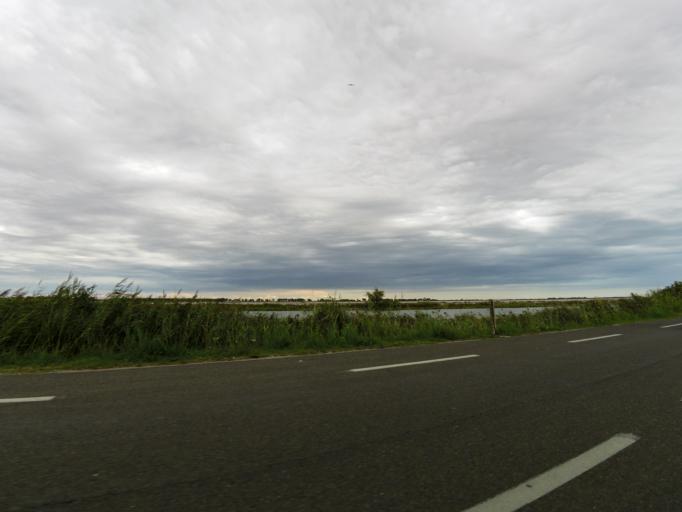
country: FR
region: Languedoc-Roussillon
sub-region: Departement du Gard
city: Le Grau-du-Roi
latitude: 43.5383
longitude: 4.1447
